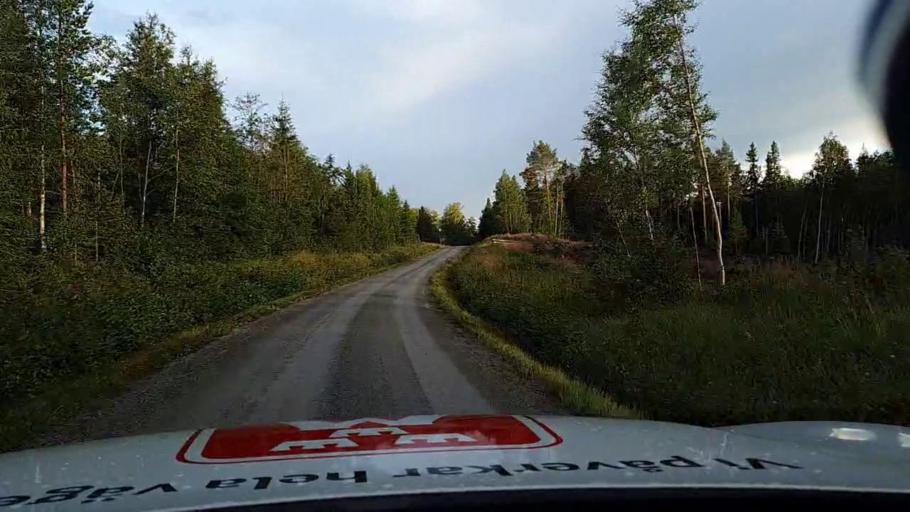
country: SE
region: Jaemtland
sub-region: Bergs Kommun
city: Hoverberg
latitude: 62.8563
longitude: 14.5358
